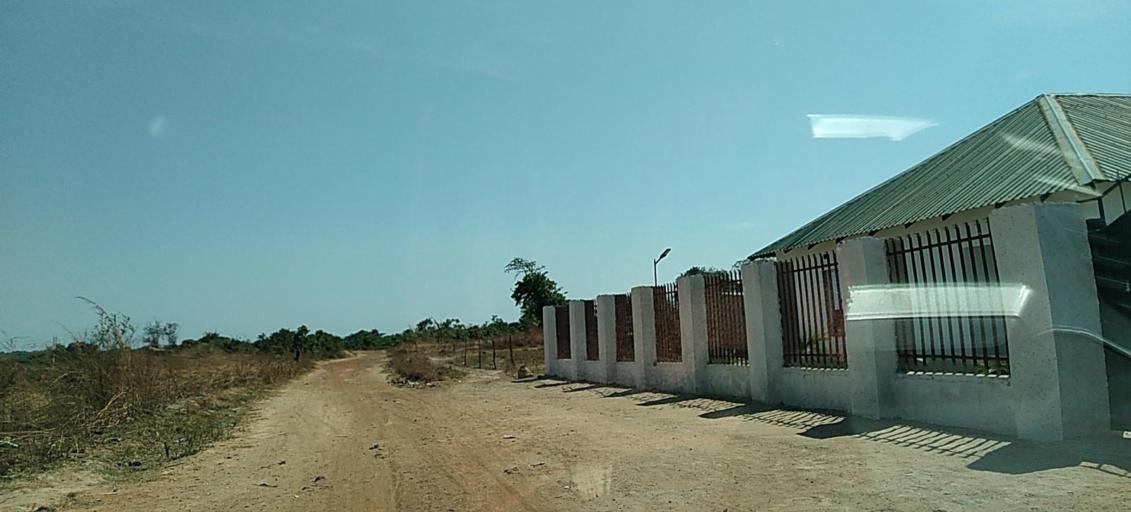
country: ZM
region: Copperbelt
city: Chililabombwe
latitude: -12.3174
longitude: 27.8631
